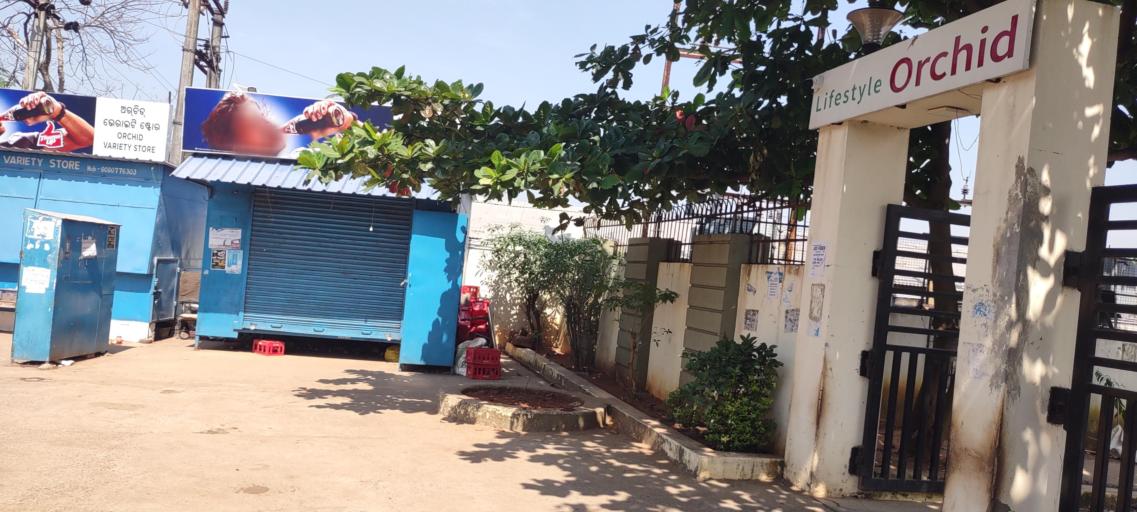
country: IN
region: Odisha
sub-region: Khordha
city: Bhubaneshwar
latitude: 20.3478
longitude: 85.7695
